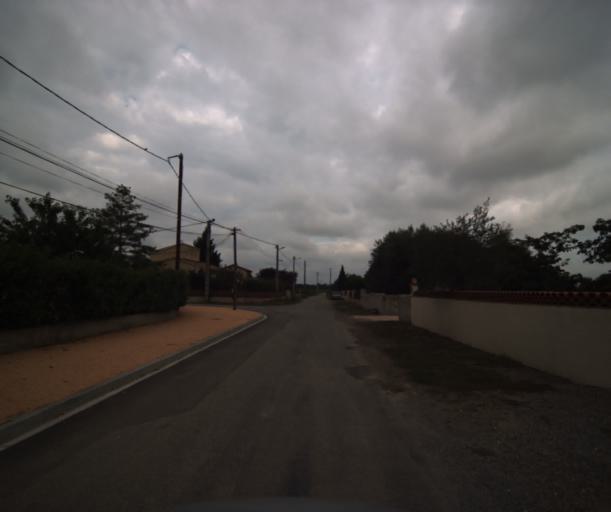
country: FR
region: Midi-Pyrenees
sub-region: Departement de la Haute-Garonne
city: Labastidette
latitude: 43.4453
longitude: 1.2920
